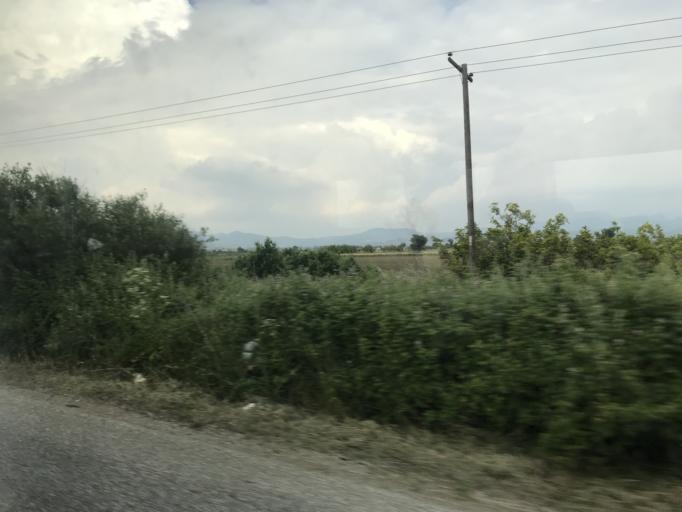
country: GR
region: East Macedonia and Thrace
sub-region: Nomos Rodopis
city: Sapes
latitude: 40.9774
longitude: 25.6469
